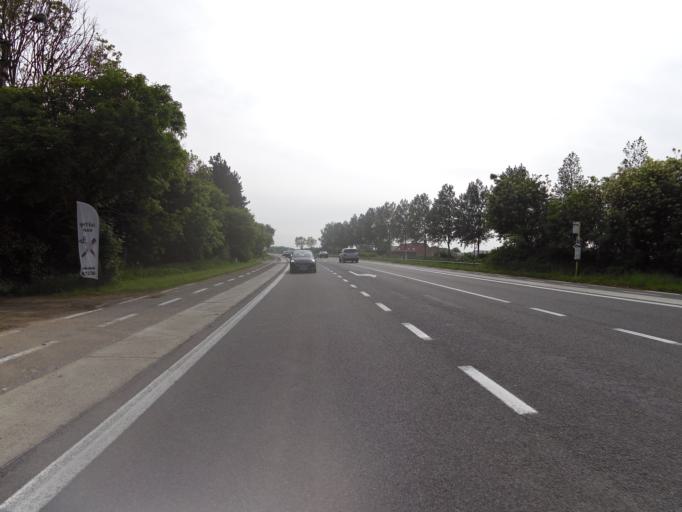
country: BE
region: Flanders
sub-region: Provincie West-Vlaanderen
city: Veurne
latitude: 51.0977
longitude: 2.6835
